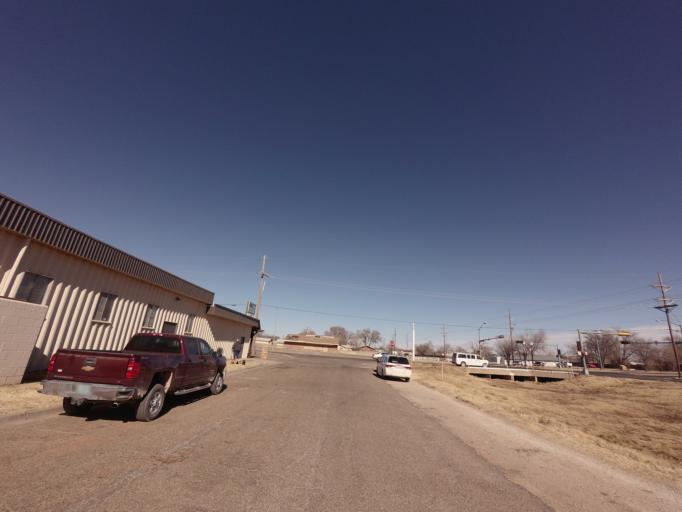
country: US
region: New Mexico
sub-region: Curry County
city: Clovis
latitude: 34.4042
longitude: -103.2322
